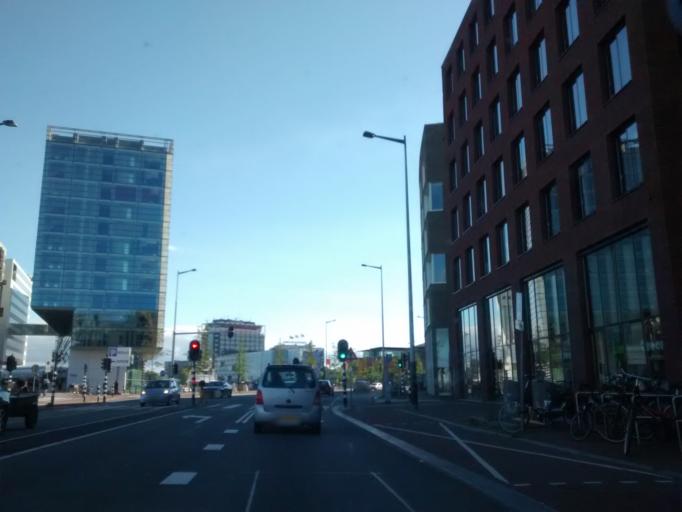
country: NL
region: North Holland
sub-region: Gemeente Amsterdam
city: Amsterdam
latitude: 52.3864
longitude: 4.8928
